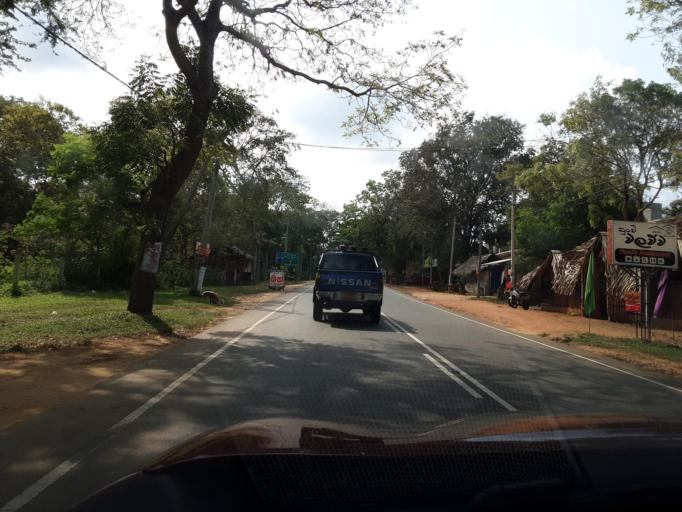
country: LK
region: Uva
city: Haputale
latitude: 6.3570
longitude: 81.1871
